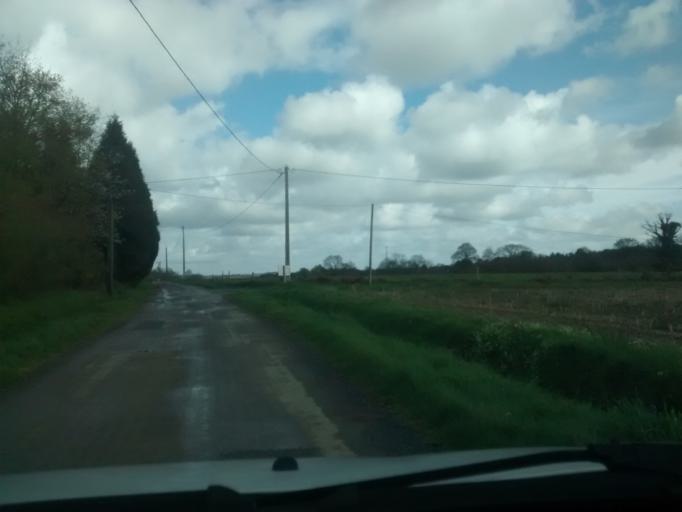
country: FR
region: Brittany
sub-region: Departement d'Ille-et-Vilaine
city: Servon-sur-Vilaine
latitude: 48.1528
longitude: -1.4911
